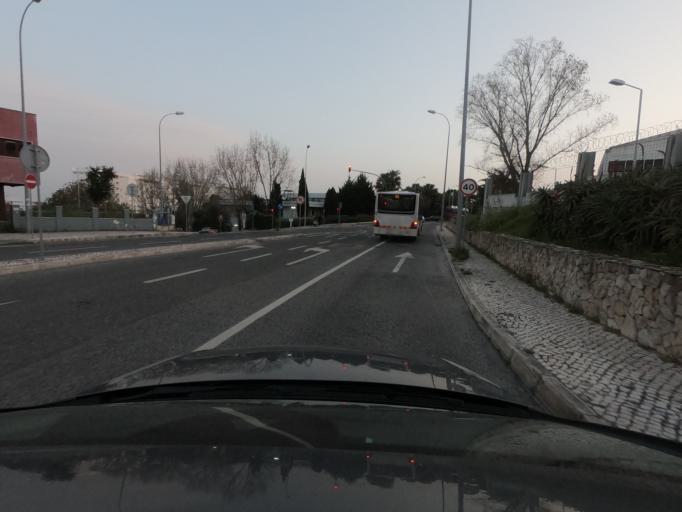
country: PT
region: Lisbon
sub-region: Amadora
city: Amadora
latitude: 38.7376
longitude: -9.2143
